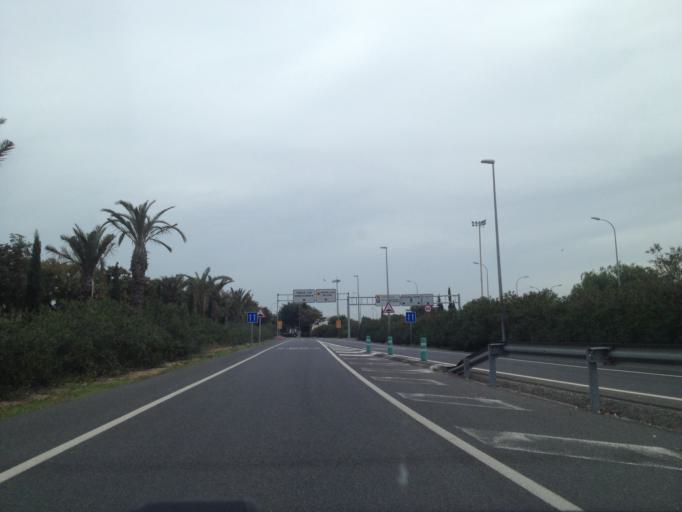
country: ES
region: Balearic Islands
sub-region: Illes Balears
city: s'Arenal
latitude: 39.5446
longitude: 2.7250
